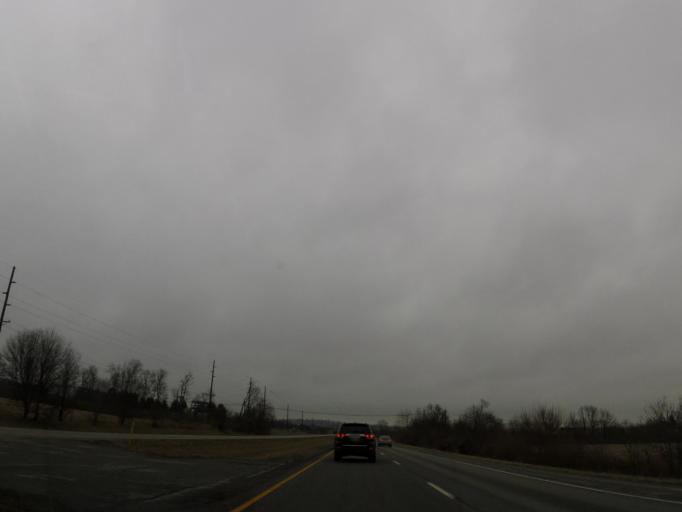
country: US
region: Kentucky
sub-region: Boyle County
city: Danville
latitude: 37.6374
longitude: -84.8017
